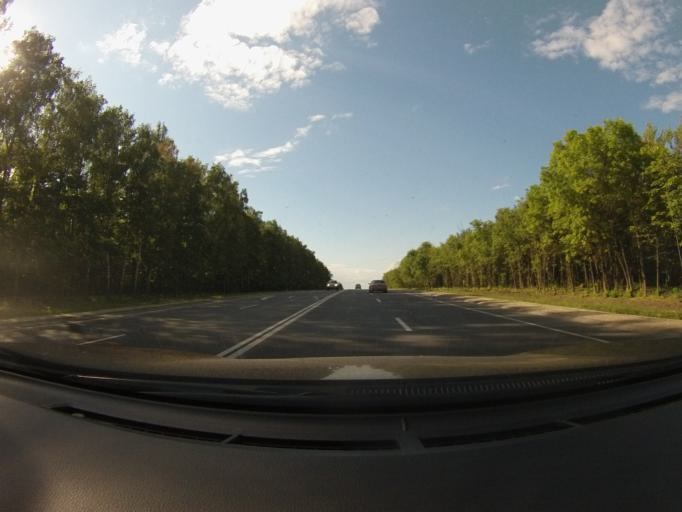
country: RU
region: Tula
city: Gorelki
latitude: 54.3125
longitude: 37.5660
